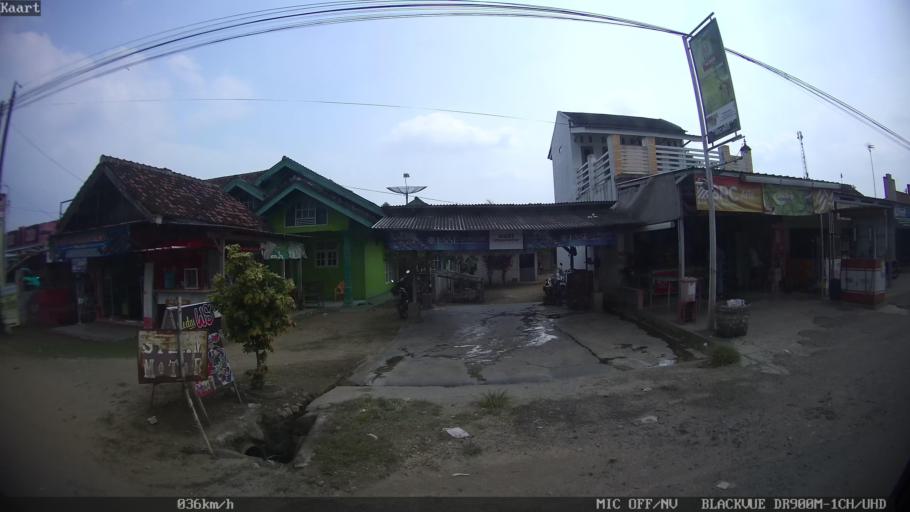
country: ID
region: Lampung
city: Gadingrejo
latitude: -5.3702
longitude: 105.0564
